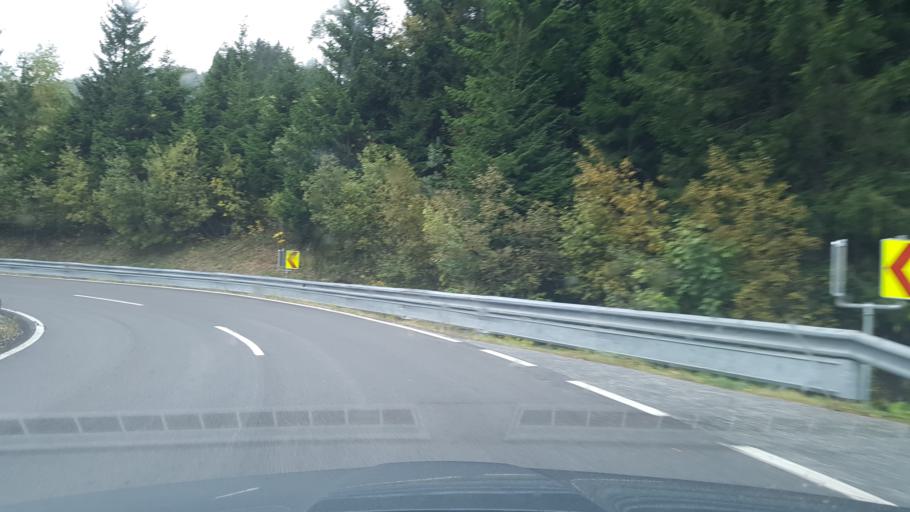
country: AT
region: Styria
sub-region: Politischer Bezirk Voitsberg
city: Salla
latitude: 47.1132
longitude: 14.9266
